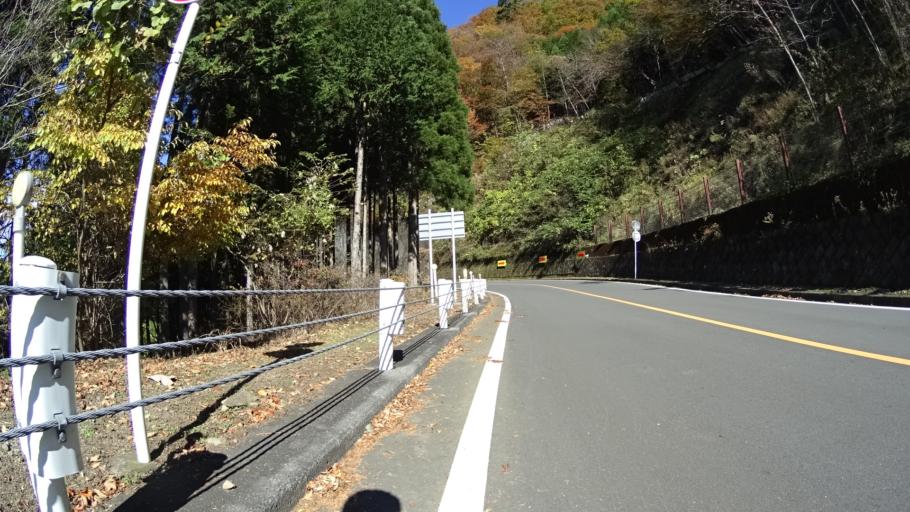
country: JP
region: Yamanashi
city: Uenohara
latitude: 35.7636
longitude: 139.0347
